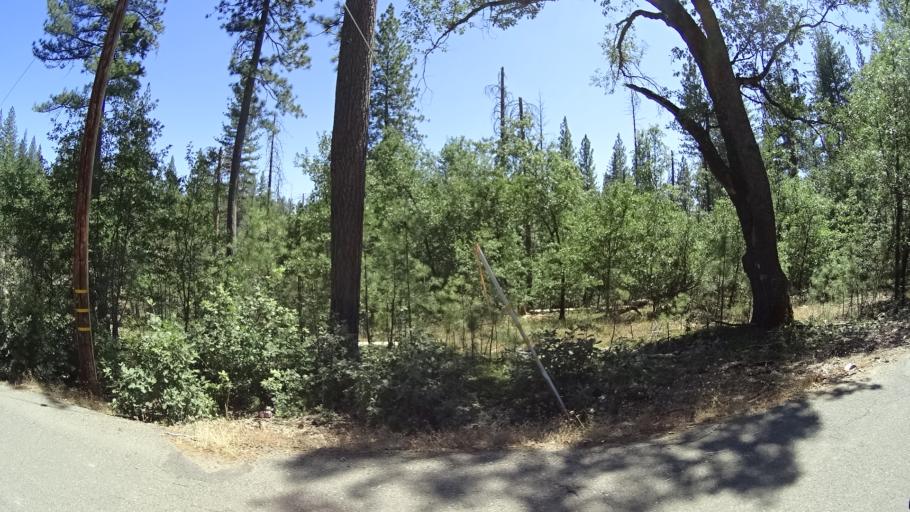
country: US
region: California
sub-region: Calaveras County
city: Mountain Ranch
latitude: 38.3203
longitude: -120.5217
